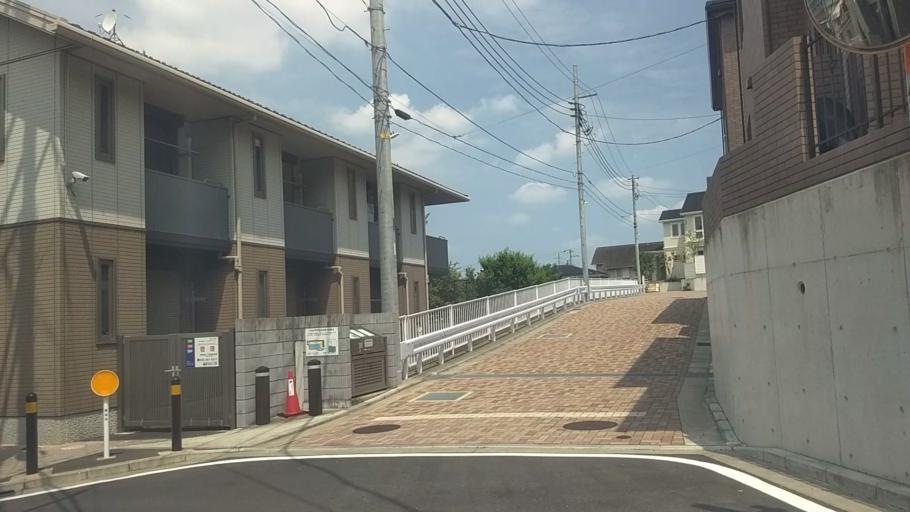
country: JP
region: Kanagawa
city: Yokohama
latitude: 35.5106
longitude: 139.6234
